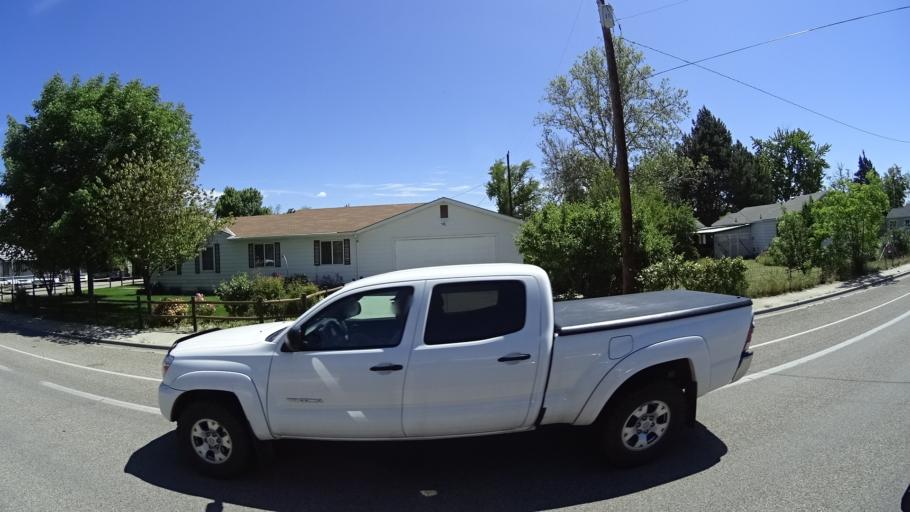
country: US
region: Idaho
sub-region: Ada County
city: Boise
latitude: 43.5820
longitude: -116.1836
